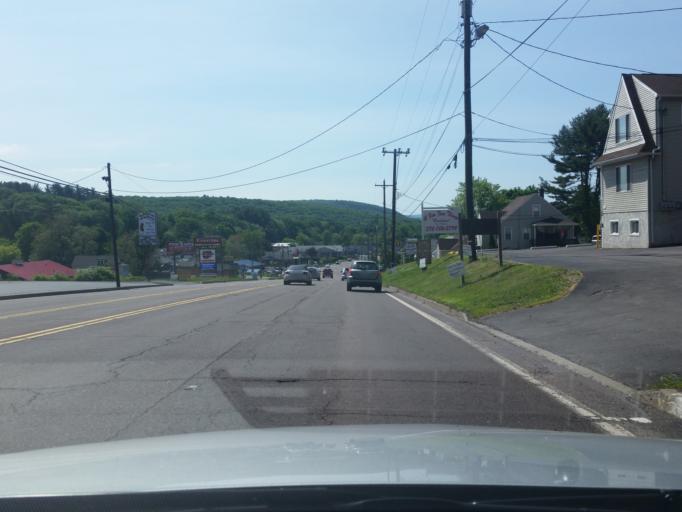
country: US
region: Pennsylvania
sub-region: Luzerne County
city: Shavertown
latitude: 41.3255
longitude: -75.9450
